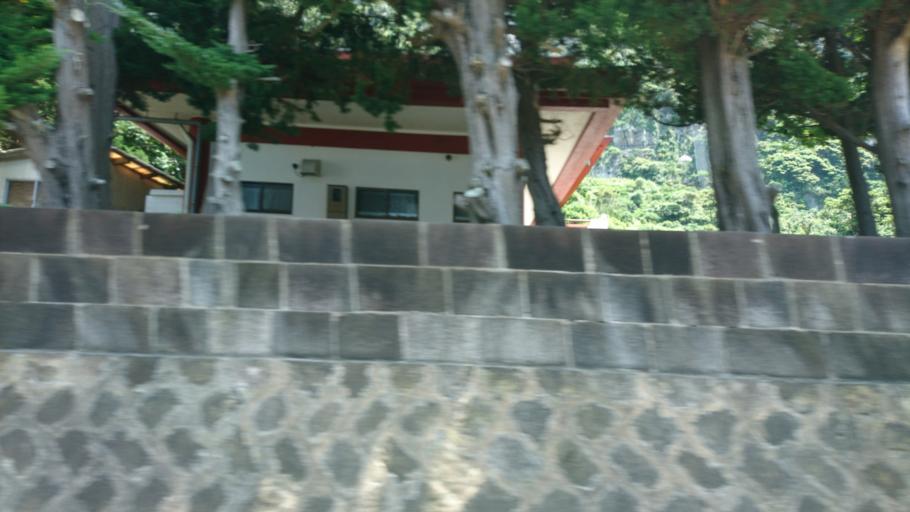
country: JP
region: Shizuoka
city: Shimoda
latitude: 34.4204
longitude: 139.2822
